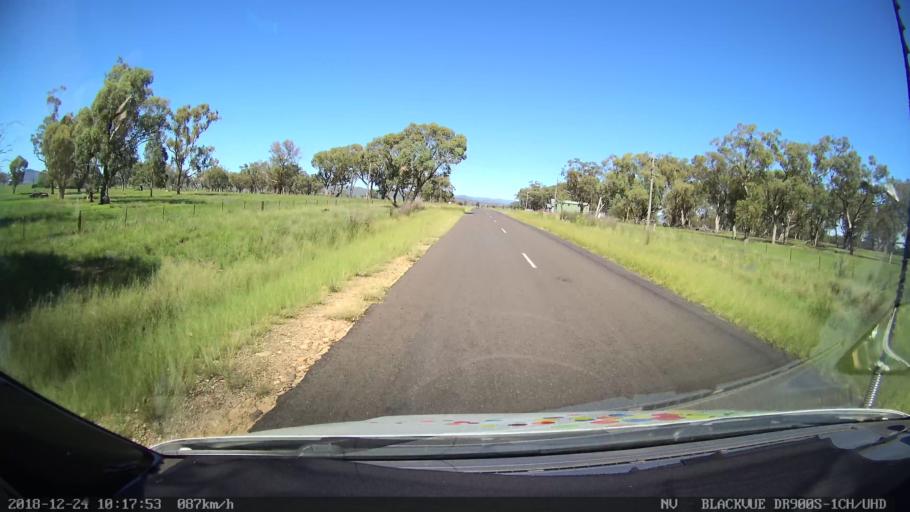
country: AU
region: New South Wales
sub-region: Liverpool Plains
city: Quirindi
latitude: -31.7217
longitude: 150.5847
